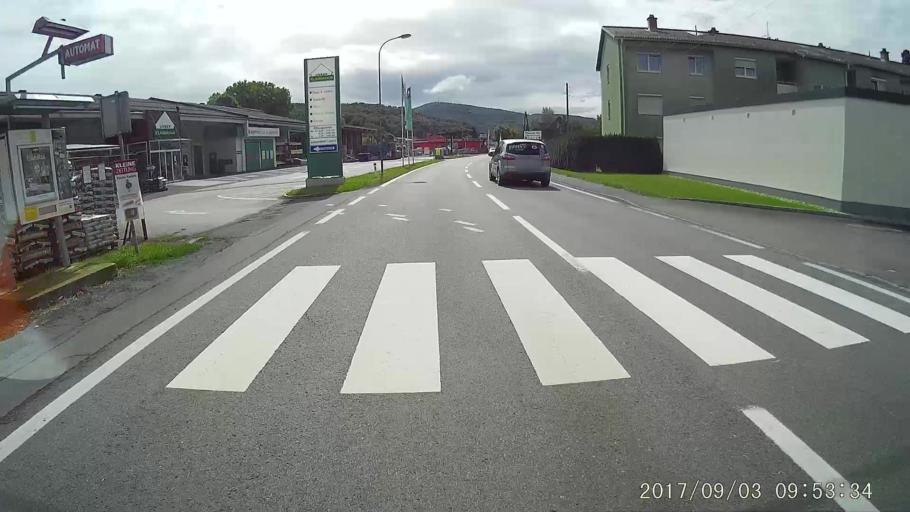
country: AT
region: Styria
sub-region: Politischer Bezirk Suedoststeiermark
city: Bad Gleichenberg
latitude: 46.8731
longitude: 15.9013
